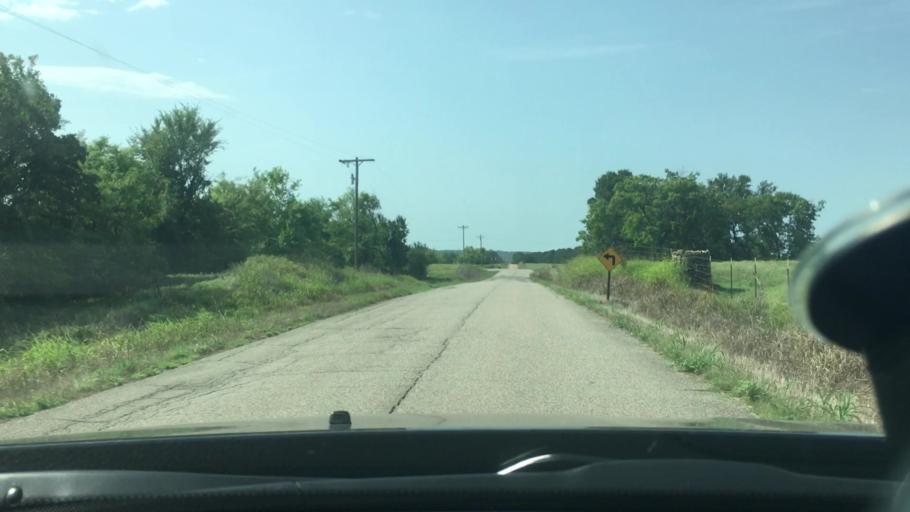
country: US
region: Oklahoma
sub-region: Atoka County
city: Atoka
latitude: 34.4637
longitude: -96.0407
